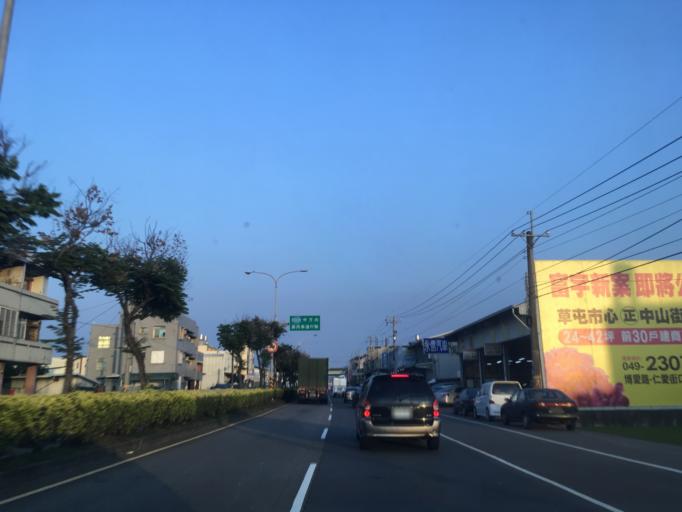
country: TW
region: Taiwan
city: Zhongxing New Village
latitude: 23.9997
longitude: 120.6592
